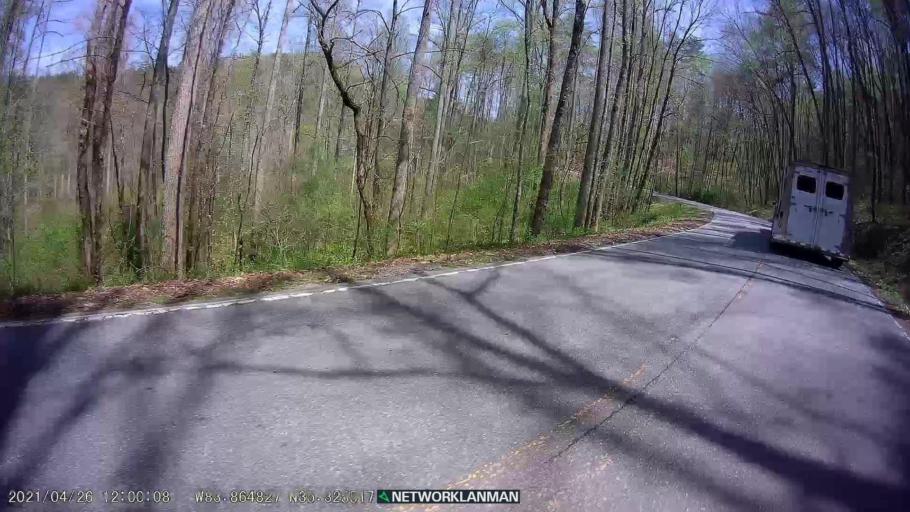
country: US
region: North Carolina
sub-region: Graham County
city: Robbinsville
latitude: 35.3255
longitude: -83.8647
